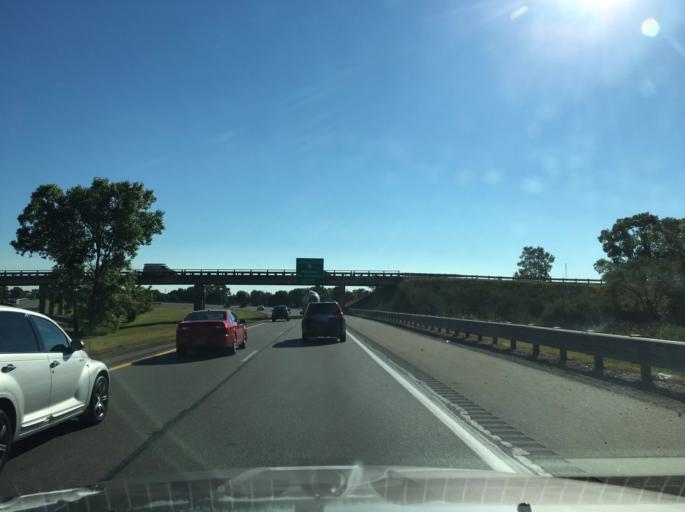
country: US
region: Michigan
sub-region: Macomb County
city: Utica
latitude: 42.6054
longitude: -83.0172
